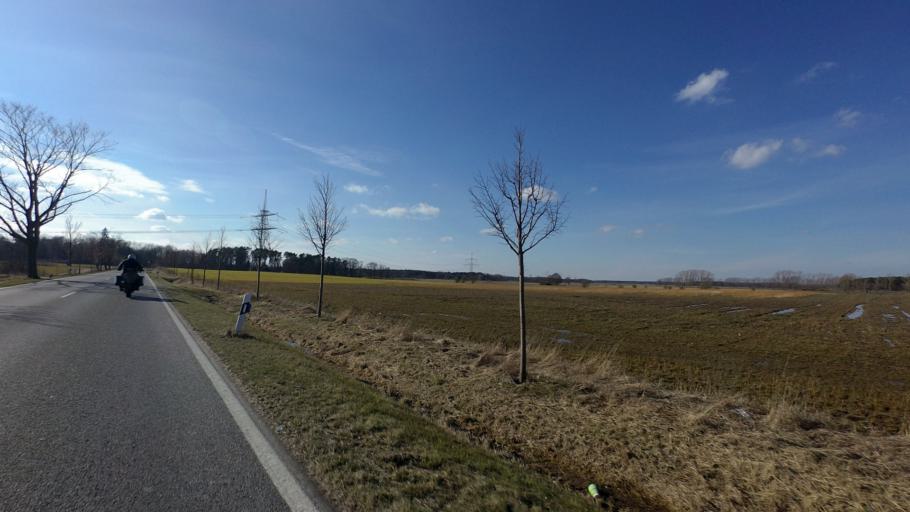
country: DE
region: Brandenburg
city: Wandlitz
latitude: 52.7556
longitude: 13.3597
